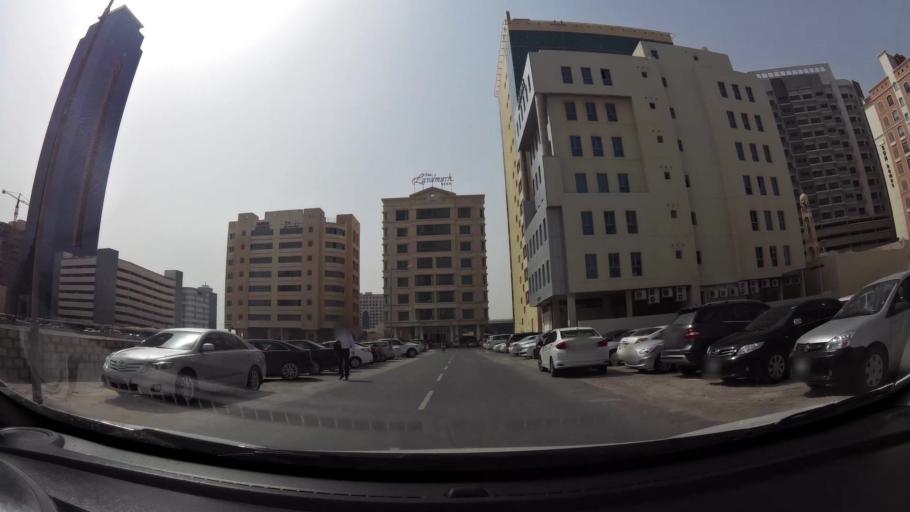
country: BH
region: Manama
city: Jidd Hafs
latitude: 26.2371
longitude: 50.5399
